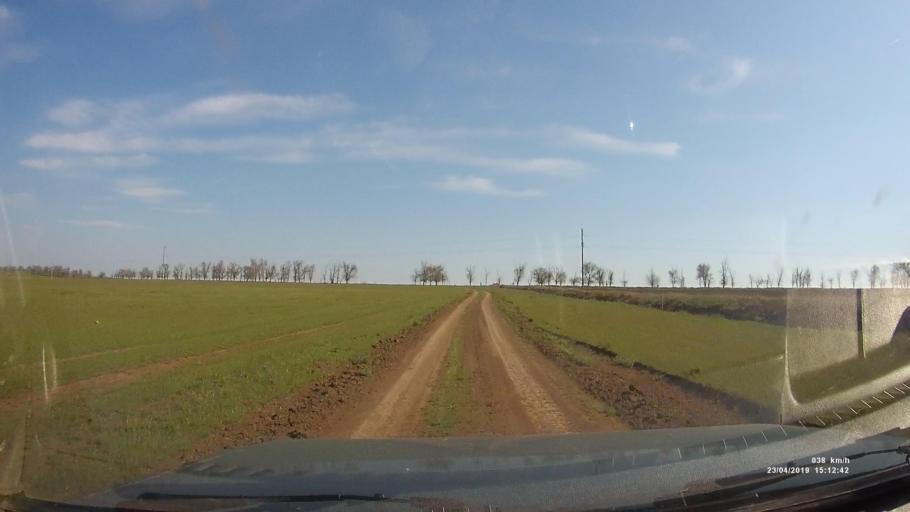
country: RU
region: Rostov
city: Remontnoye
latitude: 46.5425
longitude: 42.9508
